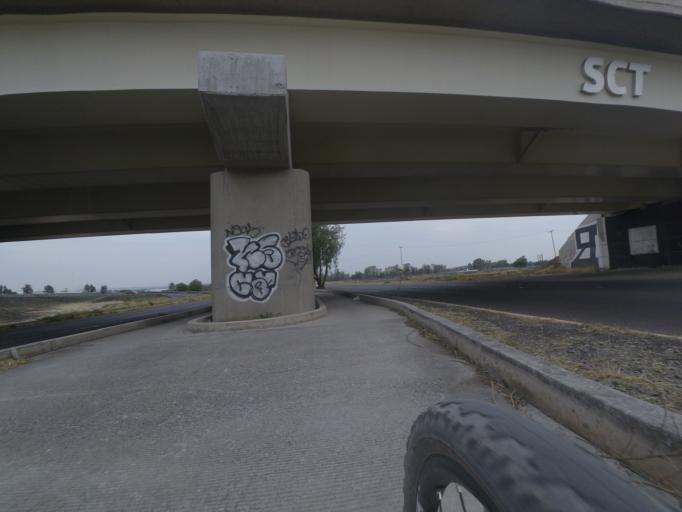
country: MX
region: Aguascalientes
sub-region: Aguascalientes
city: La Loma de los Negritos
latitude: 21.8634
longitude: -102.3713
